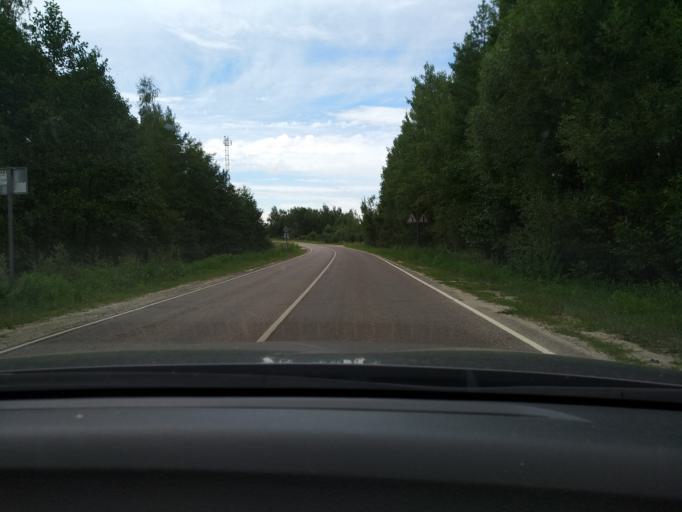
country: RU
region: Moskovskaya
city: Krasnyy Tkach
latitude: 55.3788
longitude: 39.2062
